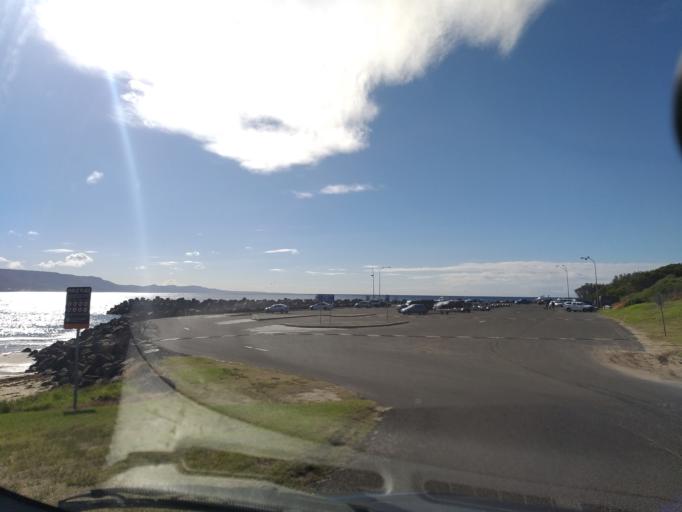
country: AU
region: New South Wales
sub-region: Wollongong
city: East Corrimal
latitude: -34.3691
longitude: 150.9277
